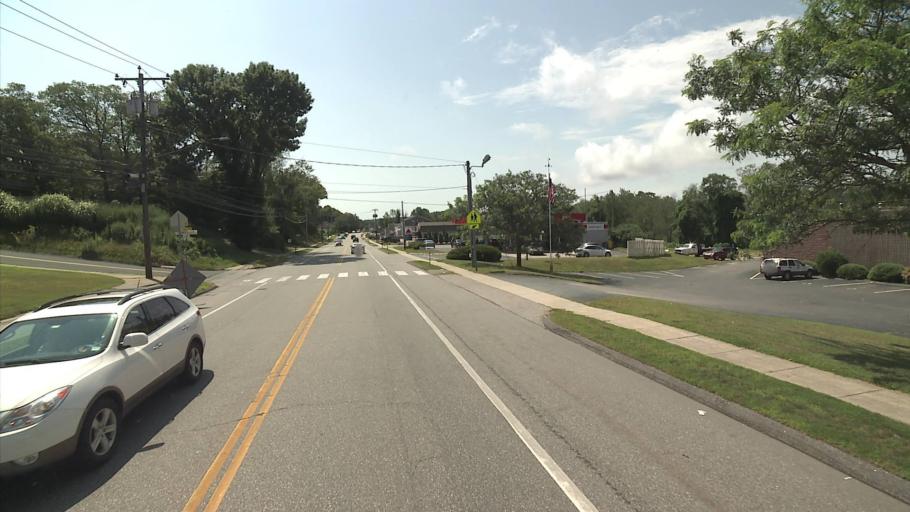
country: US
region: Connecticut
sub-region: New London County
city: Niantic
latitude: 41.3531
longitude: -72.2105
